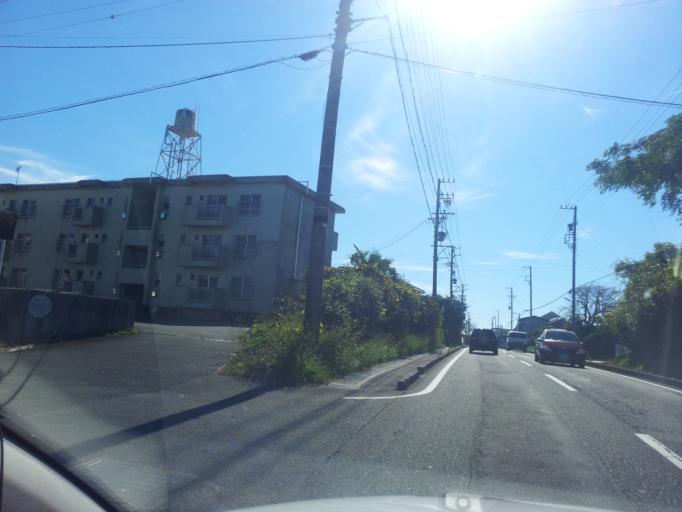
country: JP
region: Shizuoka
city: Kanaya
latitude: 34.8082
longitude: 138.1353
